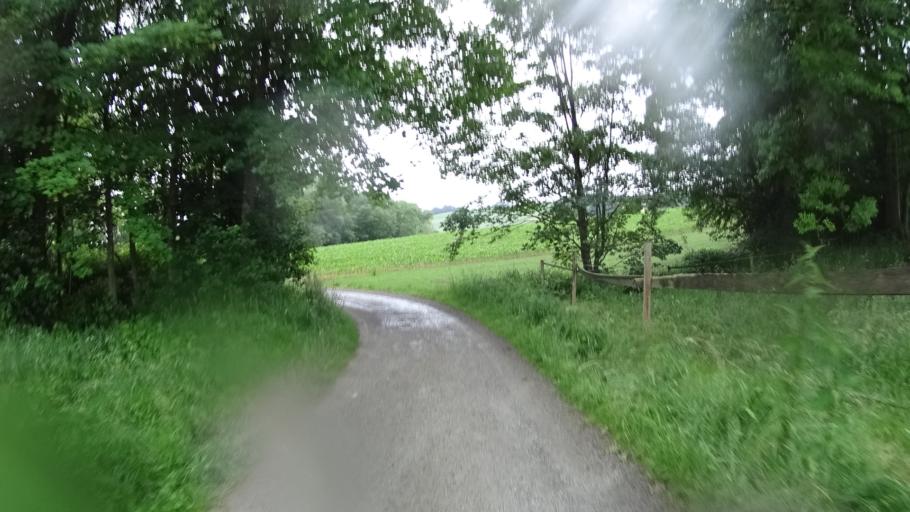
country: AT
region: Upper Austria
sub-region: Politischer Bezirk Scharding
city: Scharding
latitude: 48.4731
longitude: 13.4304
